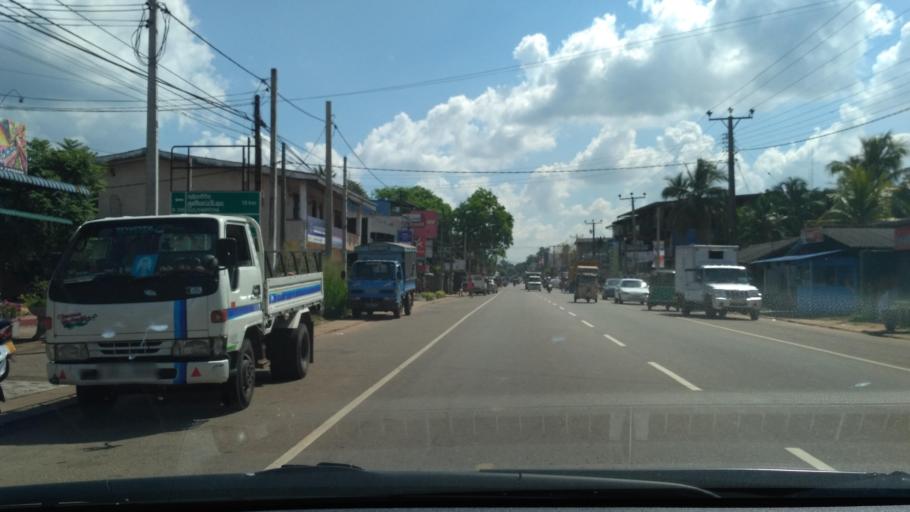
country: LK
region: North Western
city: Kuliyapitiya
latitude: 7.3297
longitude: 80.0205
